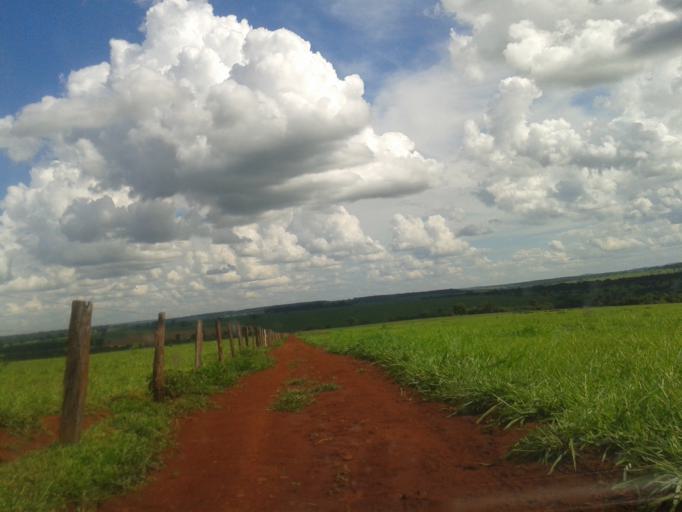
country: BR
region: Minas Gerais
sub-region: Capinopolis
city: Capinopolis
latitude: -18.7753
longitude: -49.8267
